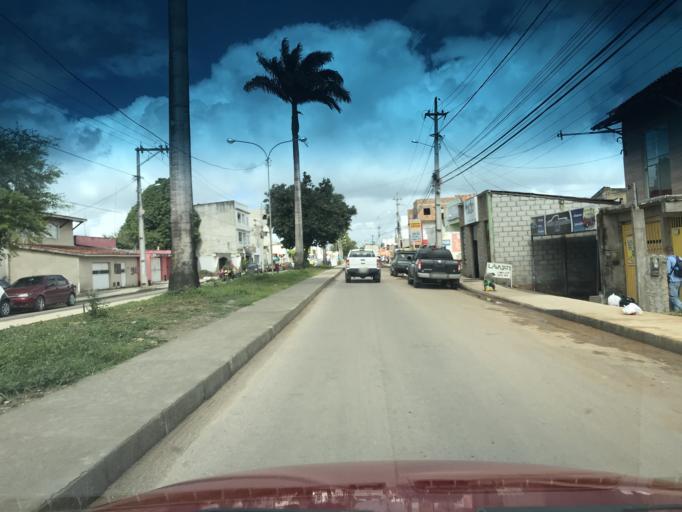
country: BR
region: Bahia
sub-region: Santo Antonio De Jesus
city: Santo Antonio de Jesus
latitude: -12.9716
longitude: -39.2725
